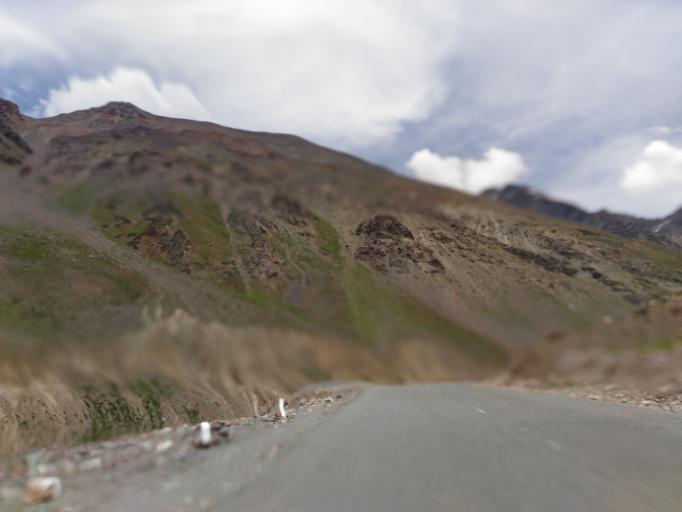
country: IN
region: Himachal Pradesh
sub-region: Lahul and Spiti
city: Kyelang
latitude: 32.7914
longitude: 77.2974
